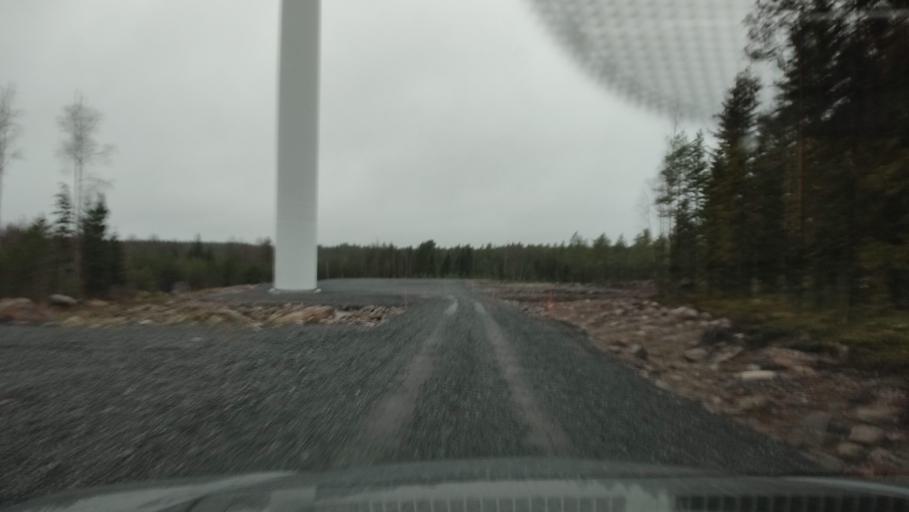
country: FI
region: Southern Ostrobothnia
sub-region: Suupohja
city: Karijoki
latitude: 62.1495
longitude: 21.6143
